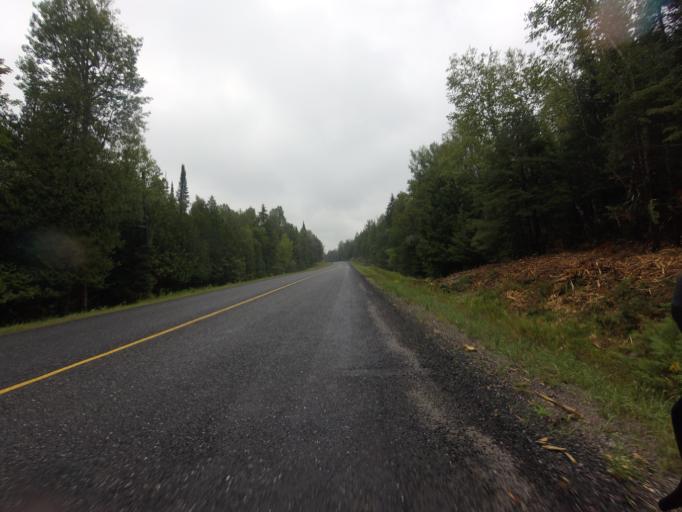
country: CA
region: Ontario
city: Perth
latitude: 45.0772
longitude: -76.4853
